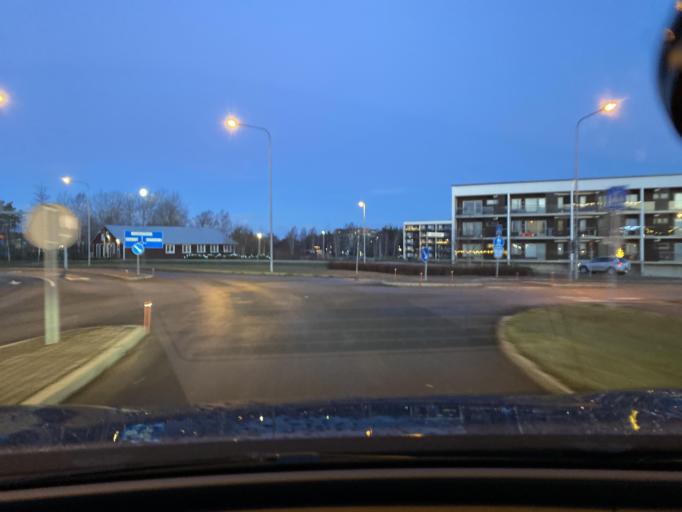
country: FI
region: Satakunta
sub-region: Rauma
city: Rauma
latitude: 61.1345
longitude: 21.5078
